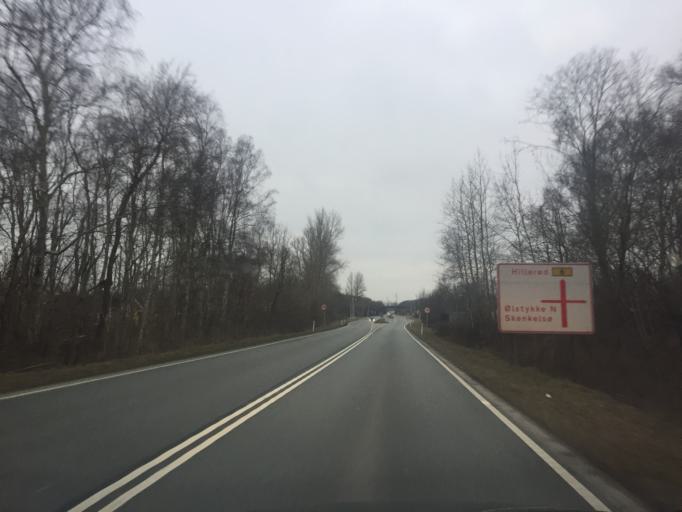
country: DK
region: Capital Region
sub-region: Egedal Kommune
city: Olstykke
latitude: 55.7977
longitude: 12.1651
